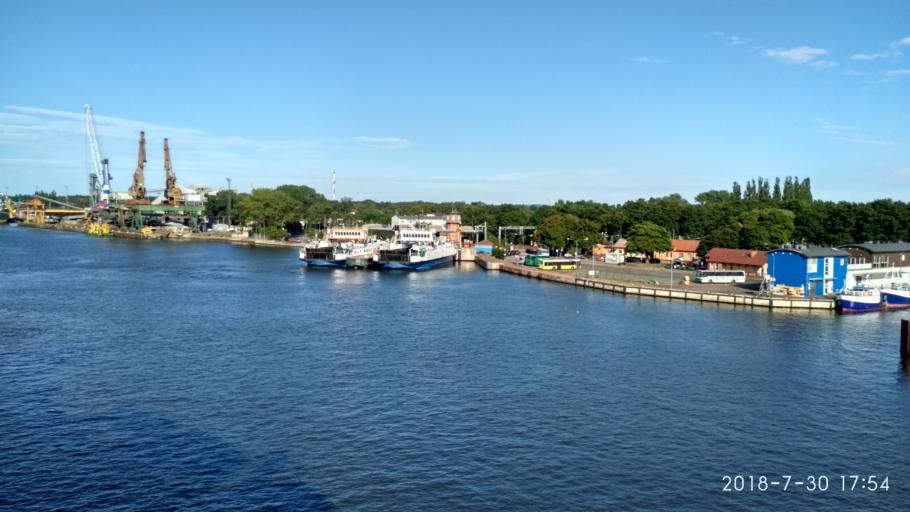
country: PL
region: West Pomeranian Voivodeship
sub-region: Swinoujscie
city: Swinoujscie
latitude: 53.9056
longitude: 14.2624
